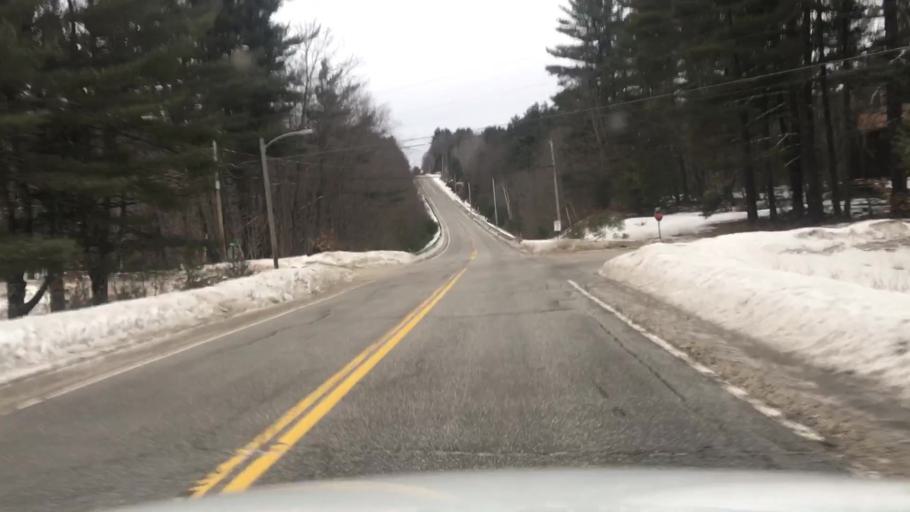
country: US
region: Maine
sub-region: York County
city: Newfield
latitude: 43.6020
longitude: -70.8837
